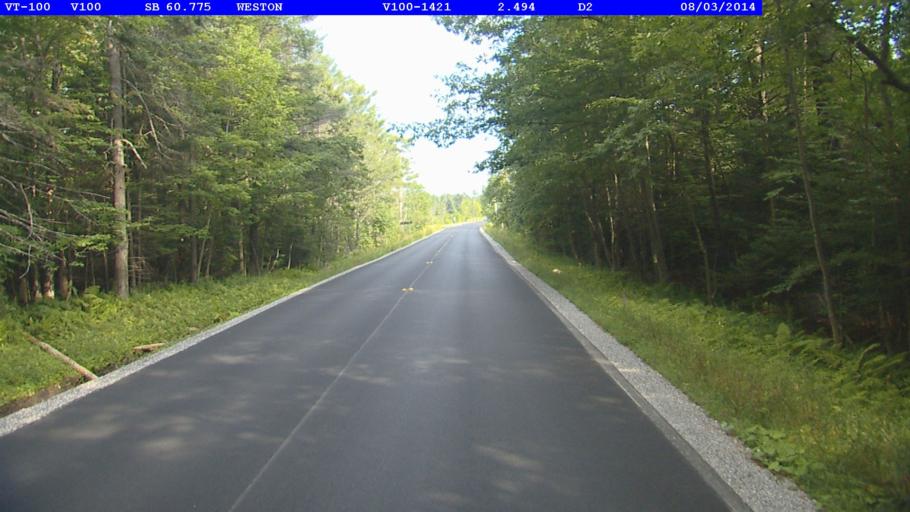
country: US
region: Vermont
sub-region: Windsor County
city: Chester
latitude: 43.2819
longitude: -72.7920
